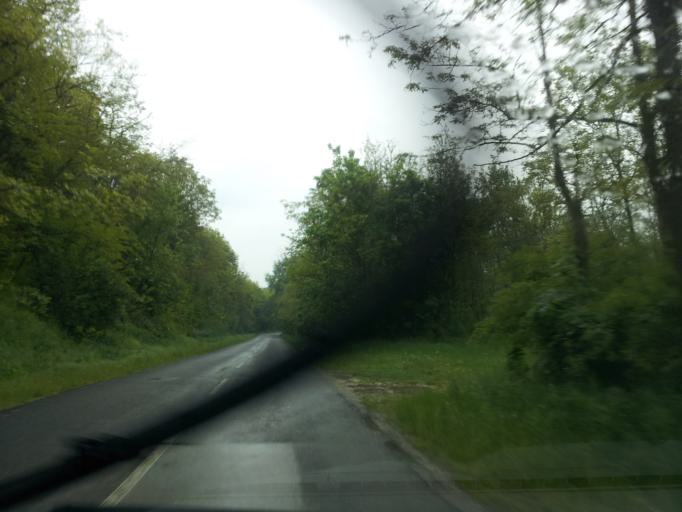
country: HU
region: Tolna
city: Bonyhad
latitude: 46.2614
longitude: 18.6091
